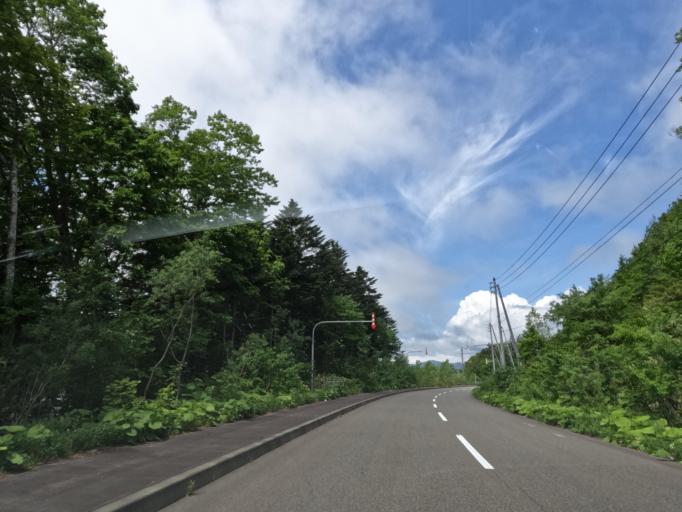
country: JP
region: Hokkaido
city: Tobetsu
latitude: 43.3487
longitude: 141.5674
